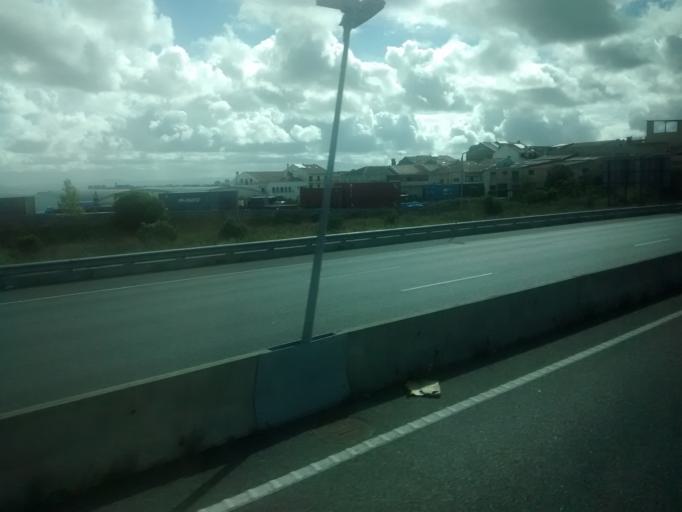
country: PT
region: Lisbon
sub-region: Loures
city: Camarate
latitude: 38.7965
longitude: -9.1417
